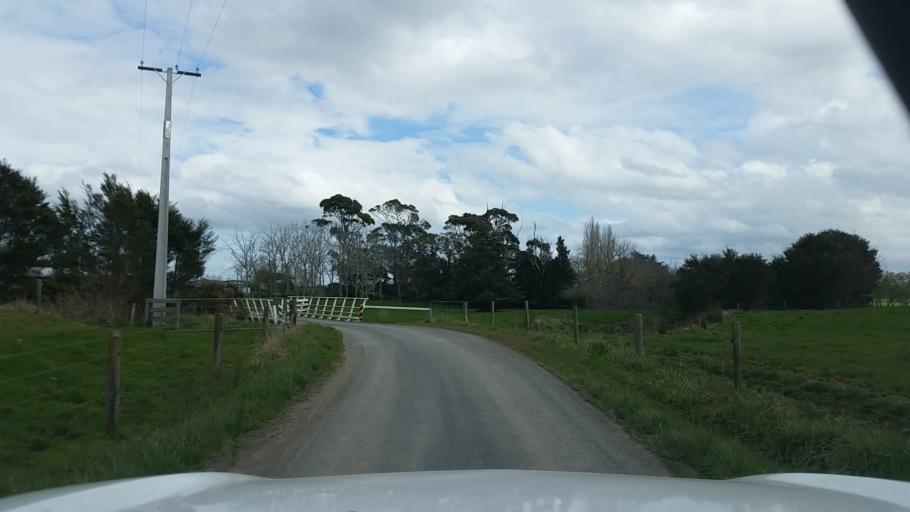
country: NZ
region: Waikato
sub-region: Hauraki District
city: Ngatea
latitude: -37.5114
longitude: 175.4404
